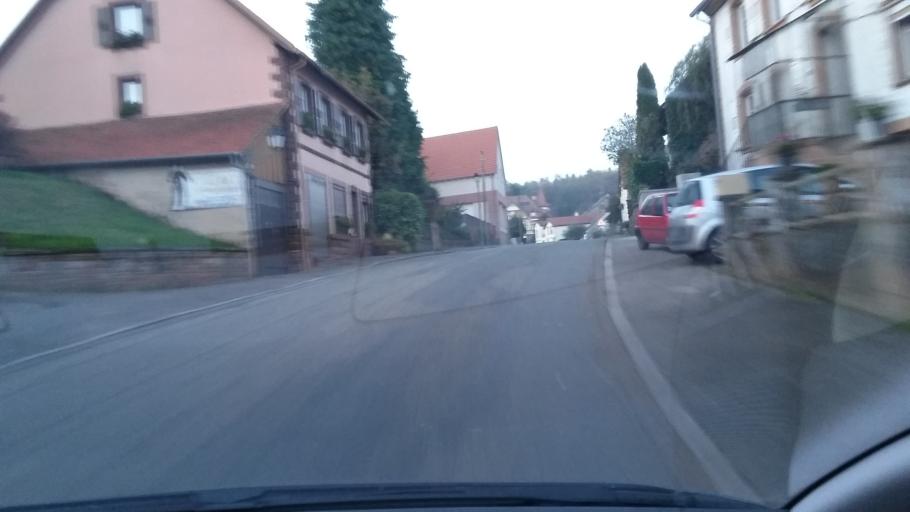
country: FR
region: Alsace
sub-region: Departement du Bas-Rhin
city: Neuwiller-les-Saverne
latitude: 48.8609
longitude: 7.3199
